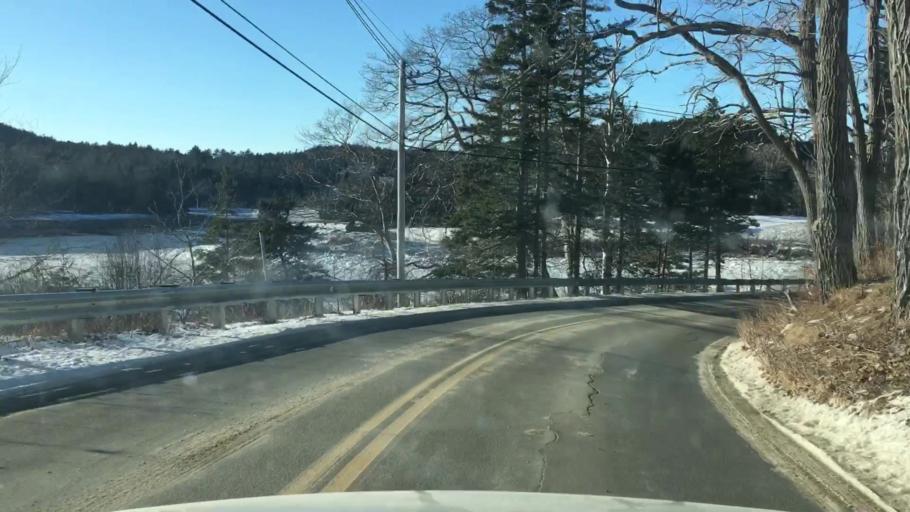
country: US
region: Maine
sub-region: Hancock County
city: Castine
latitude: 44.3492
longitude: -68.7484
